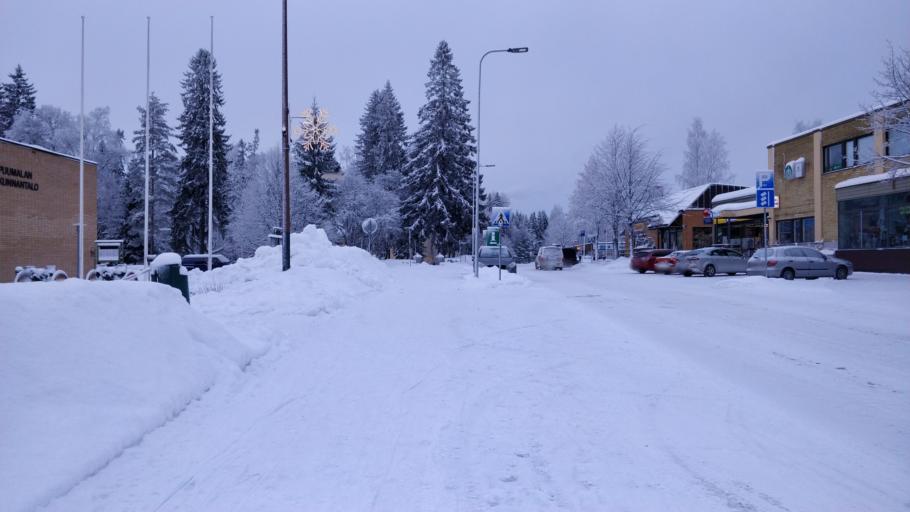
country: FI
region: Southern Savonia
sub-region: Mikkeli
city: Puumala
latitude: 61.5228
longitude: 28.1776
